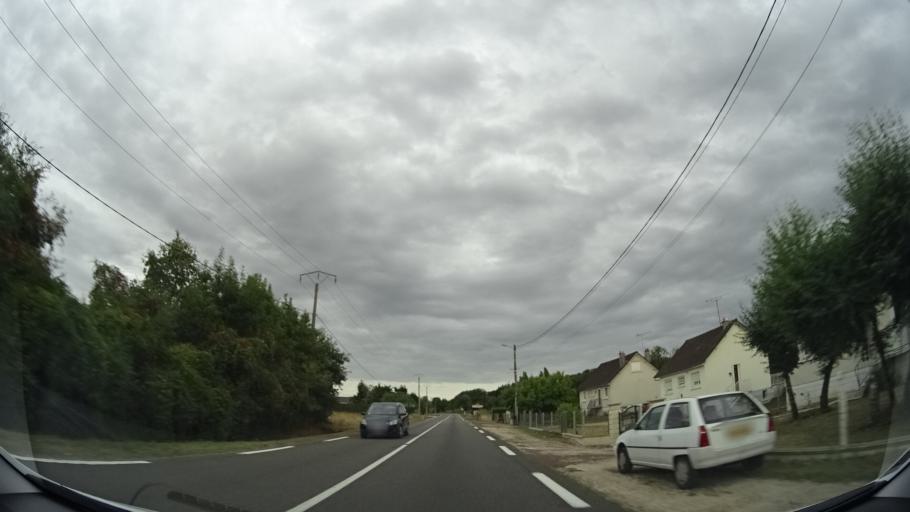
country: FR
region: Centre
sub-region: Departement du Loiret
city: Amilly
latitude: 47.9577
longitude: 2.8061
